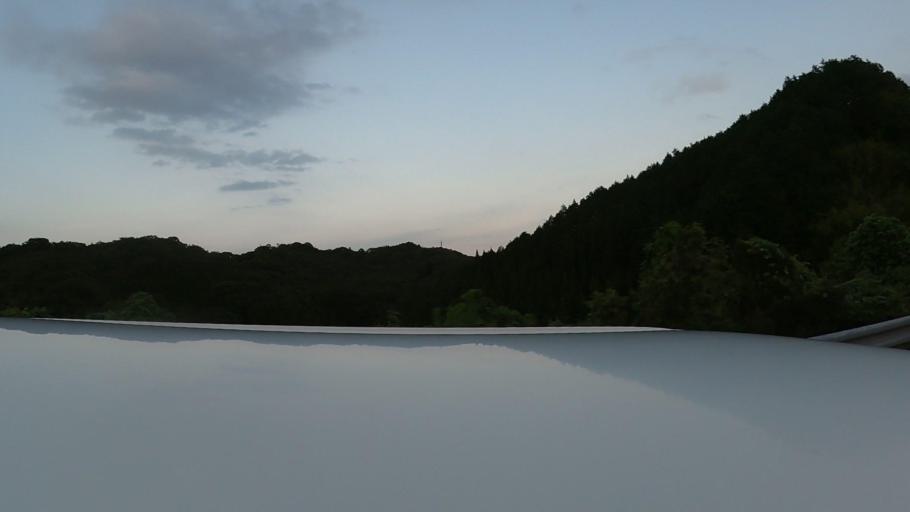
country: JP
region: Miyazaki
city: Nobeoka
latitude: 32.4546
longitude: 131.6126
